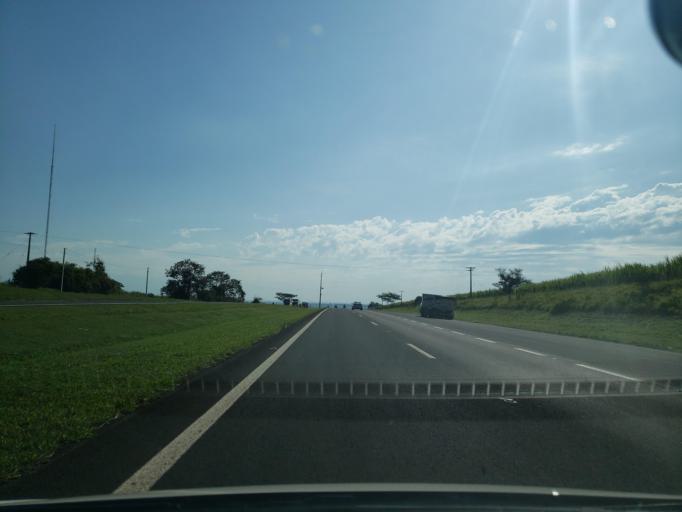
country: BR
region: Sao Paulo
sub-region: Penapolis
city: Penapolis
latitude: -21.5105
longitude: -50.0183
